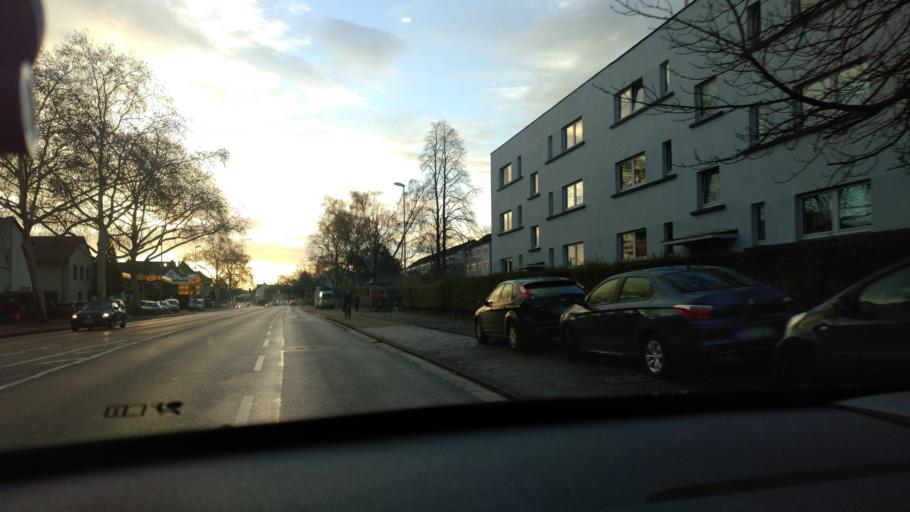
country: DE
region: North Rhine-Westphalia
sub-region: Regierungsbezirk Dusseldorf
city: Muelheim (Ruhr)
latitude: 51.4044
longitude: 6.8722
